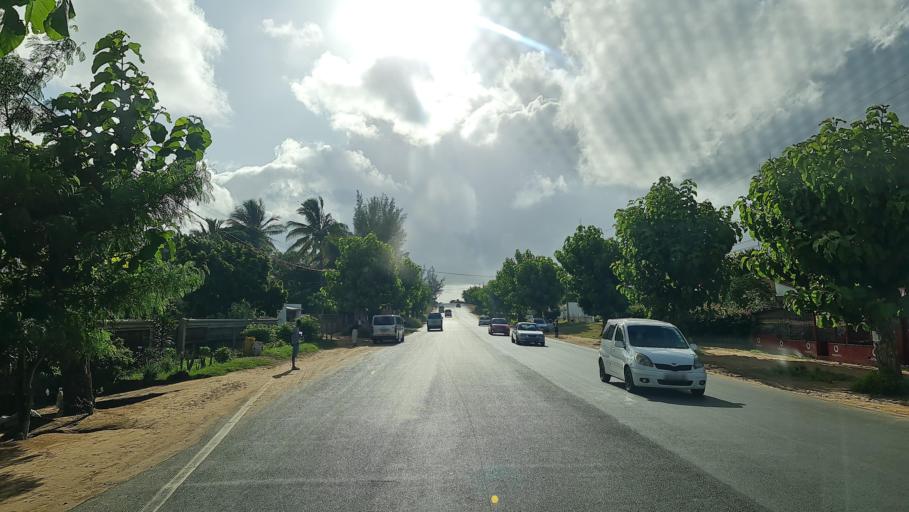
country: MZ
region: Gaza
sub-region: Xai-Xai District
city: Xai-Xai
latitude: -25.0569
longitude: 33.6577
